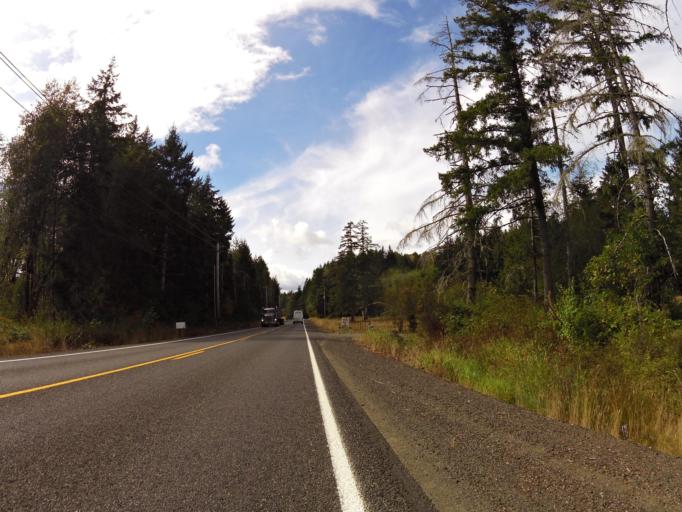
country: US
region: Washington
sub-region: Mason County
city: Shelton
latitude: 47.1572
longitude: -123.0490
